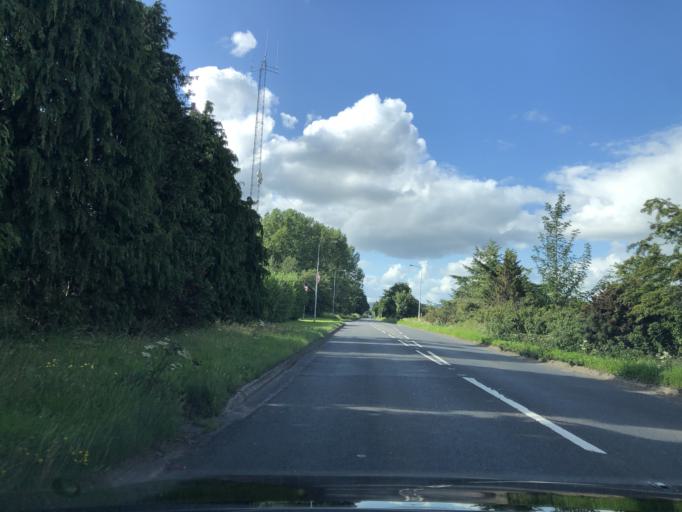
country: GB
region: Northern Ireland
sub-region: Ards District
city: Comber
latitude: 54.5527
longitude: -5.7553
